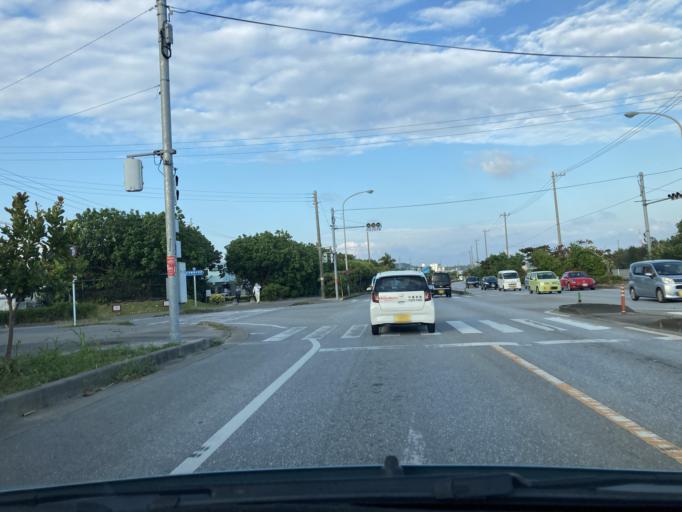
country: JP
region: Okinawa
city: Okinawa
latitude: 26.3284
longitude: 127.8356
